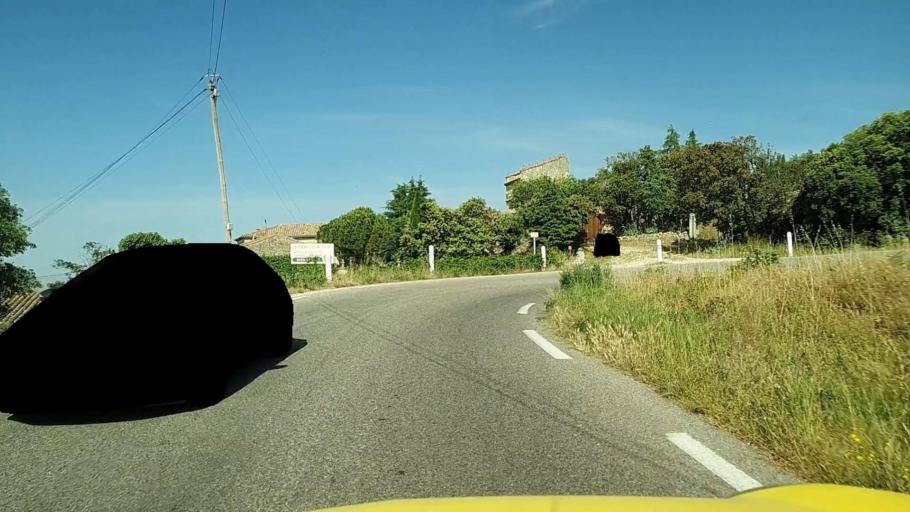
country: FR
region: Languedoc-Roussillon
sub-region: Departement du Gard
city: Montaren-et-Saint-Mediers
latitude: 44.0603
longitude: 4.3957
